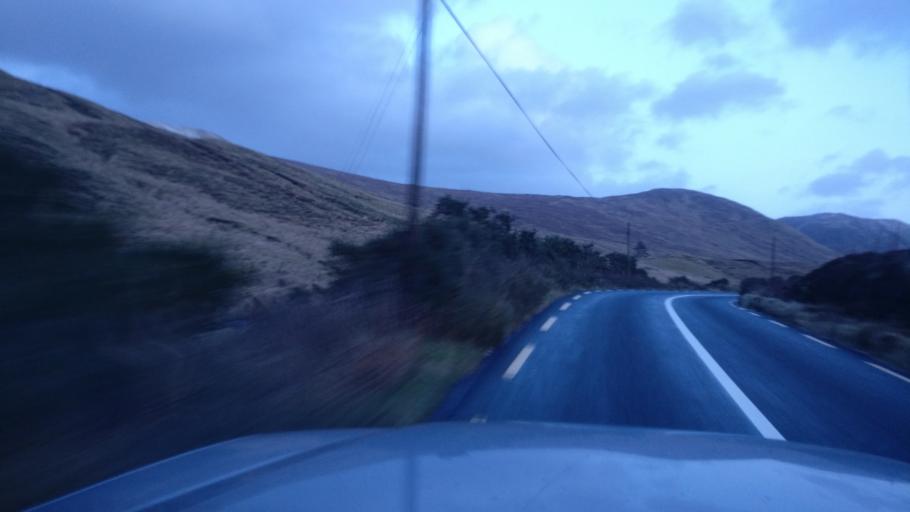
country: IE
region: Connaught
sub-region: Maigh Eo
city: Westport
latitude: 53.5855
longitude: -9.6819
